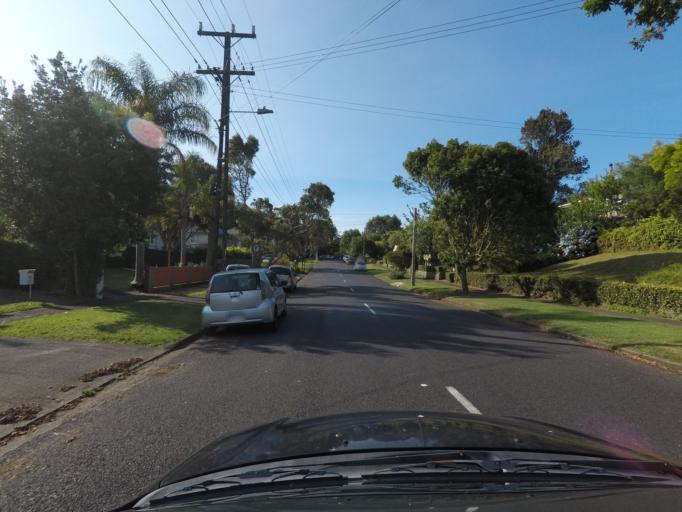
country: NZ
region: Auckland
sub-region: Auckland
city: Auckland
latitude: -36.9070
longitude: 174.7519
